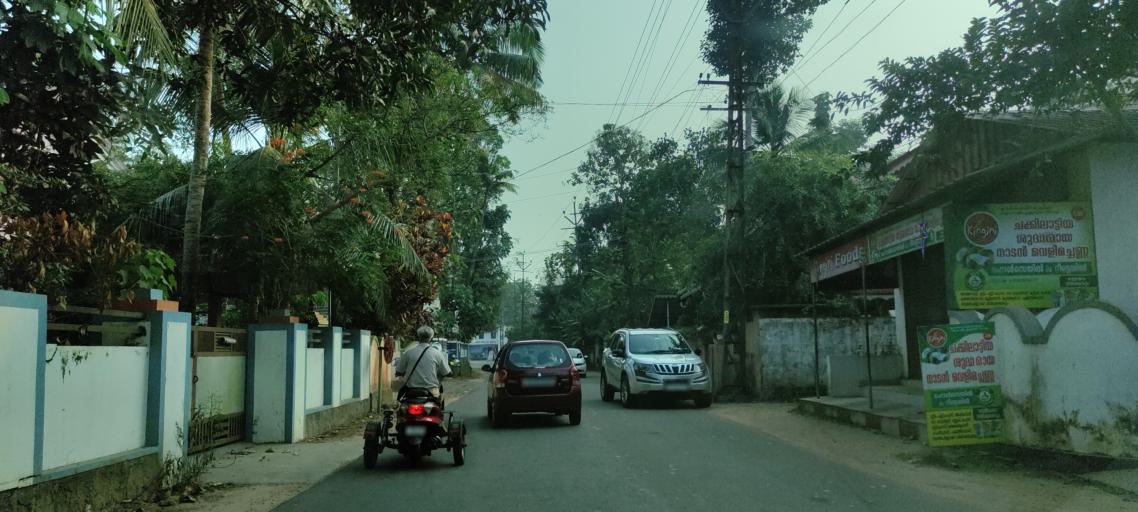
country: IN
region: Kerala
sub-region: Kottayam
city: Vaikam
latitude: 9.7106
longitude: 76.4755
